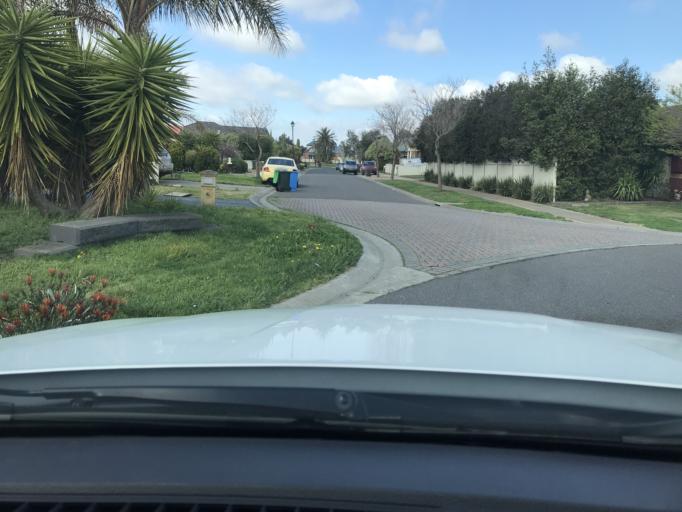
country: AU
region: Victoria
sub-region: Hume
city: Roxburgh Park
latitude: -37.6093
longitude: 144.9227
